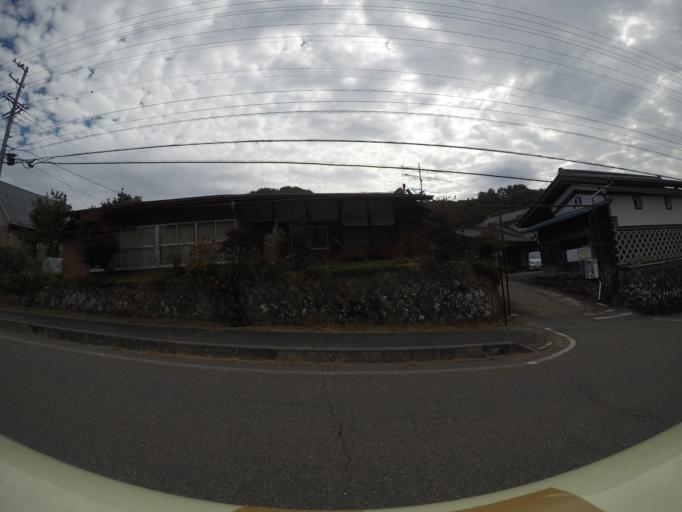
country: JP
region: Nagano
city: Chino
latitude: 35.9435
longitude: 138.1041
